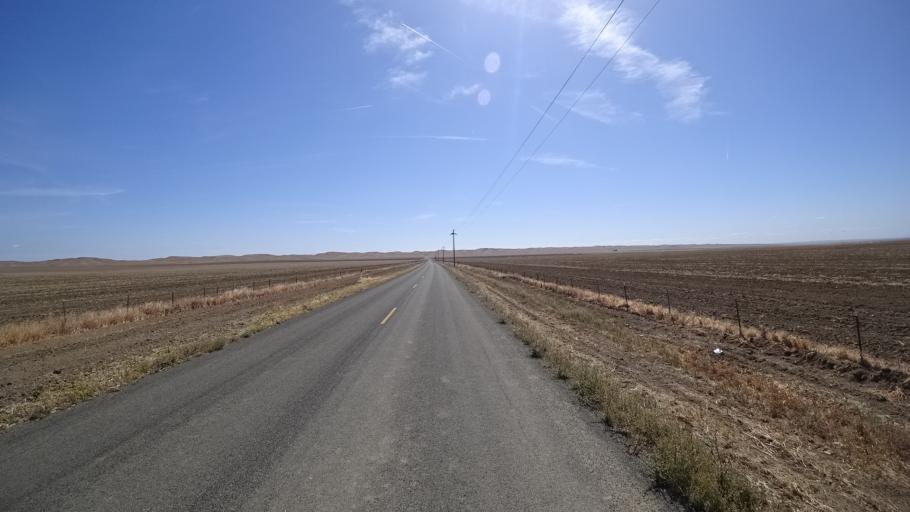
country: US
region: California
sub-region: Kings County
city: Avenal
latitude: 35.9352
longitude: -120.0560
